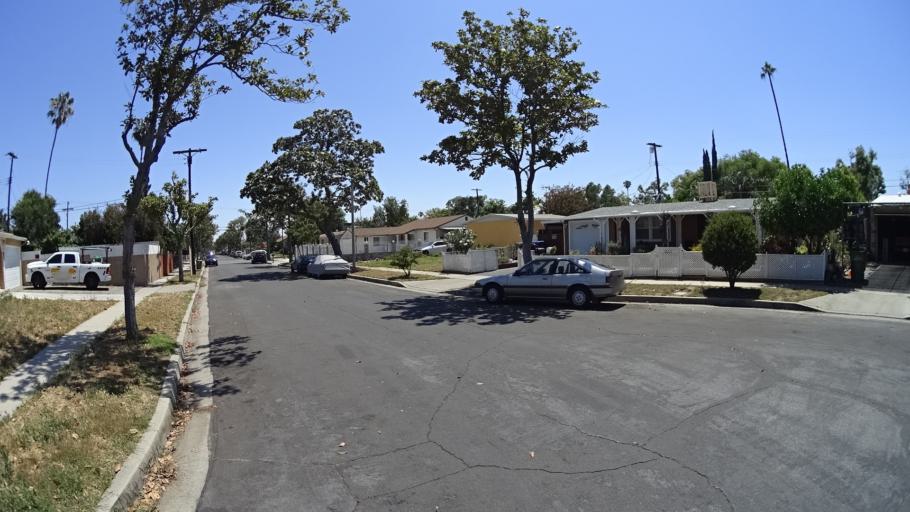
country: US
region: California
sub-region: Los Angeles County
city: Van Nuys
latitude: 34.2171
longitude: -118.4372
